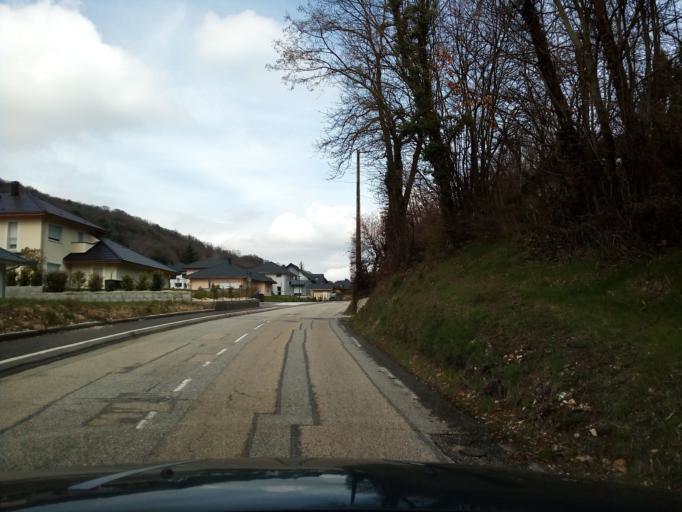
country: FR
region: Rhone-Alpes
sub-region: Departement de la Savoie
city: Saint-Baldoph
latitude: 45.5390
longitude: 5.9493
